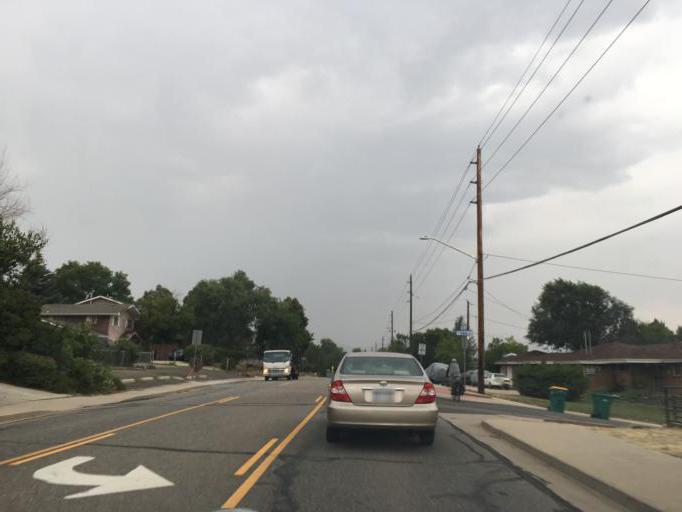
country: US
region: Colorado
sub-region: Jefferson County
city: Wheat Ridge
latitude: 39.7693
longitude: -105.1022
